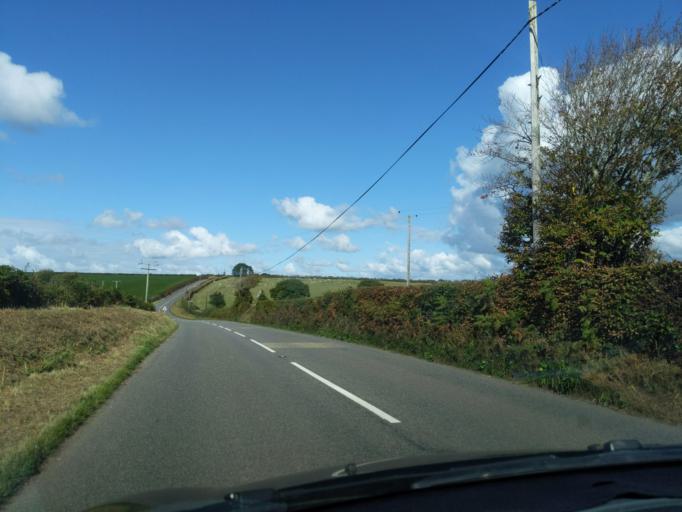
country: GB
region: England
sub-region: Cornwall
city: Boyton
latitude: 50.7163
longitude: -4.3294
